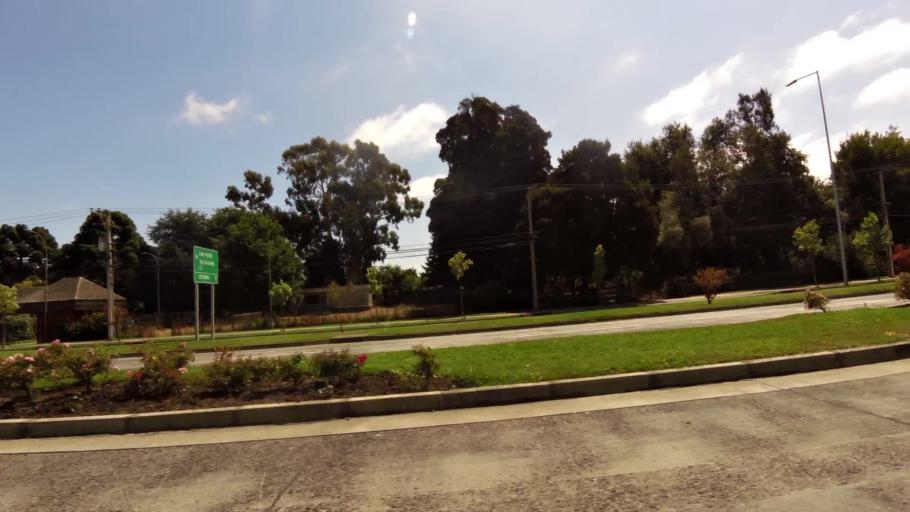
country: CL
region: Biobio
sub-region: Provincia de Concepcion
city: Concepcion
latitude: -36.7863
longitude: -73.0601
